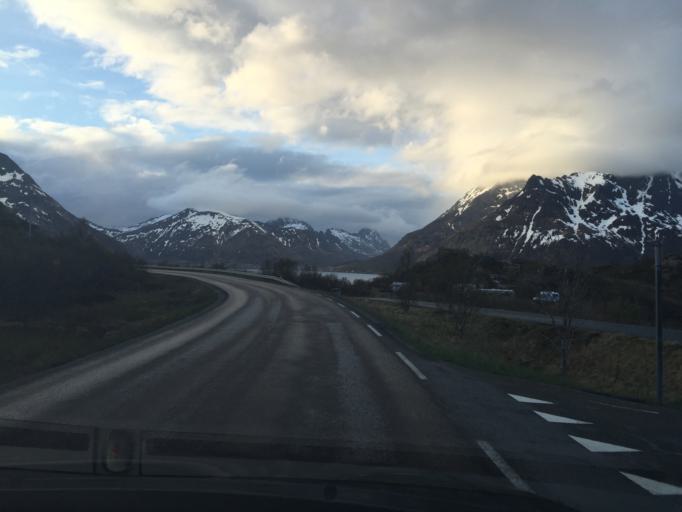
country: NO
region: Nordland
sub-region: Vagan
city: Svolvaer
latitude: 68.3149
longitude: 14.7141
